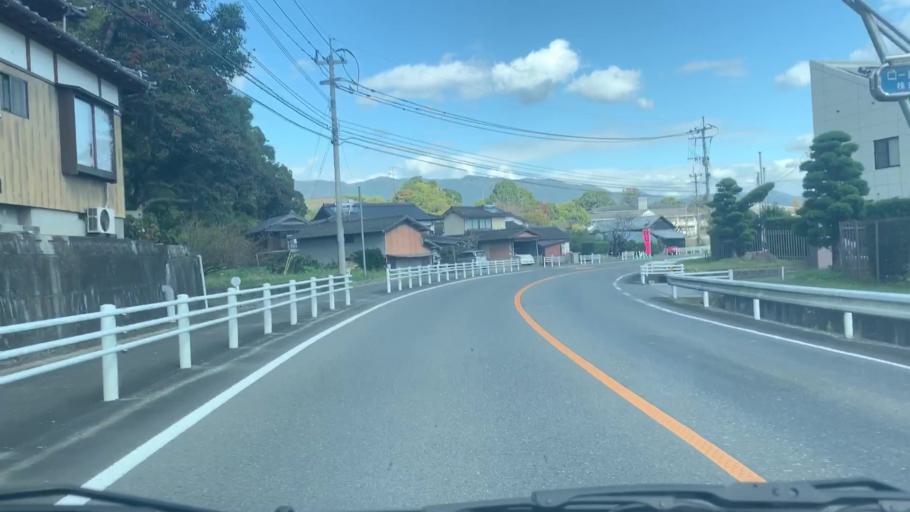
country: JP
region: Saga Prefecture
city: Saga-shi
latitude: 33.2702
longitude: 130.1808
